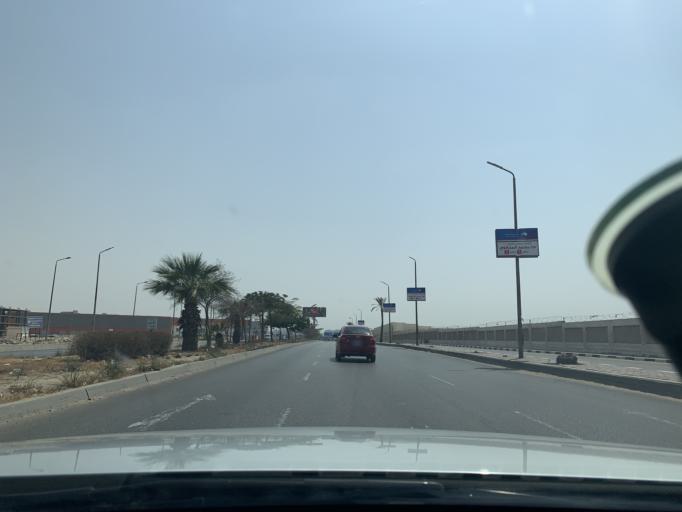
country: EG
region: Muhafazat al Qahirah
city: Cairo
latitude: 30.0855
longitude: 31.3658
